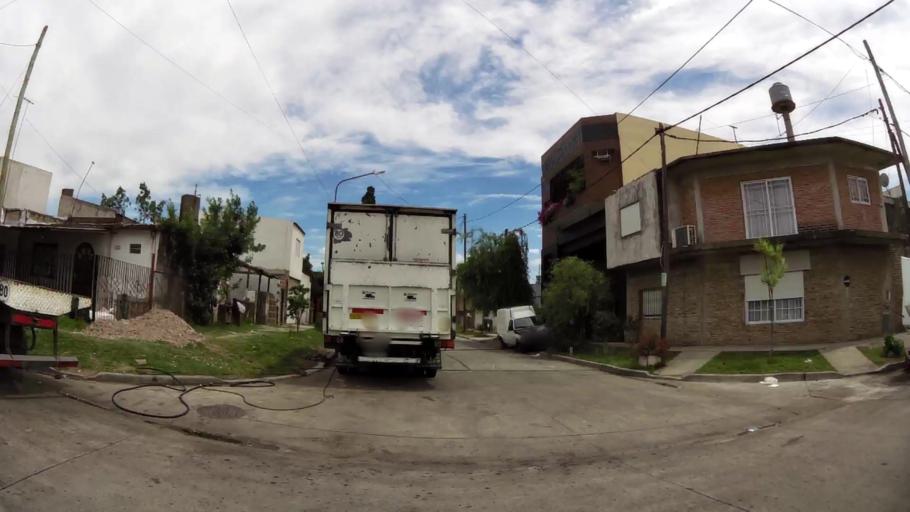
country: AR
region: Buenos Aires
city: San Justo
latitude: -34.6850
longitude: -58.5358
